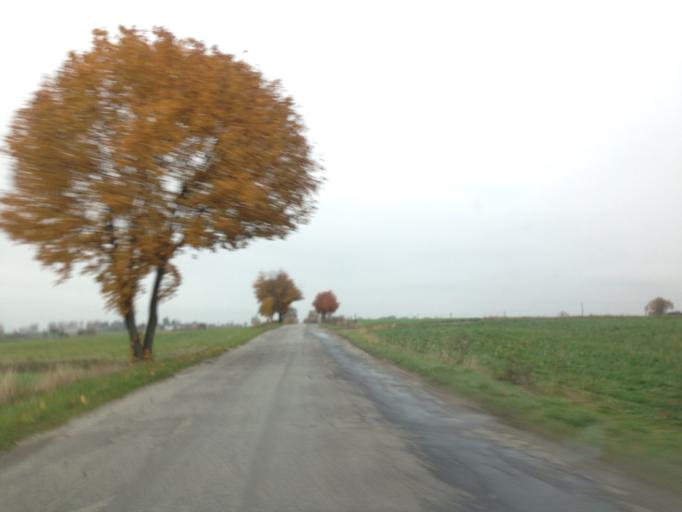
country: PL
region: Kujawsko-Pomorskie
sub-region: Powiat brodnicki
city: Bartniczka
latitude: 53.2159
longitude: 19.5873
